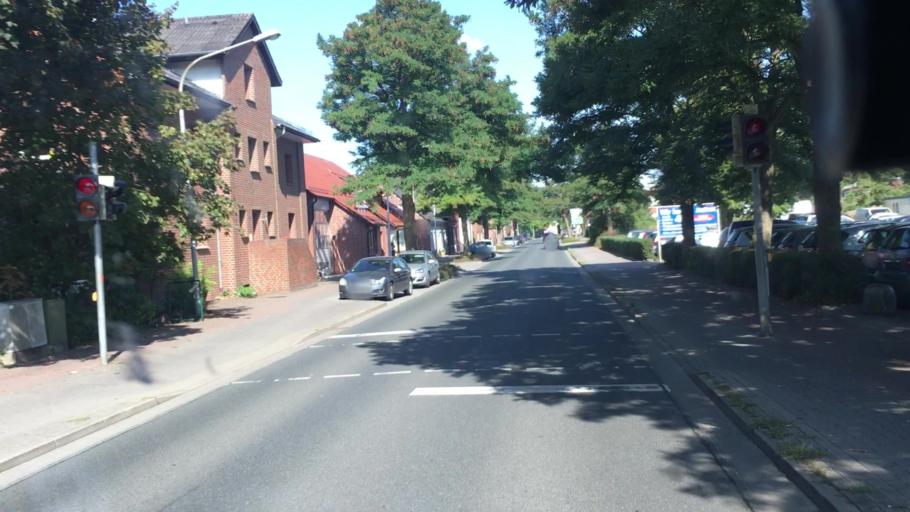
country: DE
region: Lower Saxony
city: Lohne
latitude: 52.6571
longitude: 8.2409
